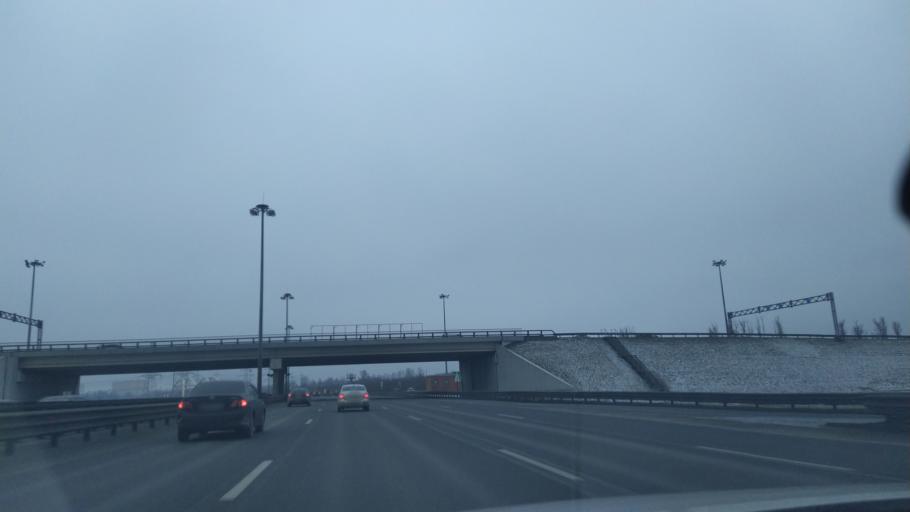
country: RU
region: St.-Petersburg
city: Krasnogvargeisky
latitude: 59.9911
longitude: 30.4821
